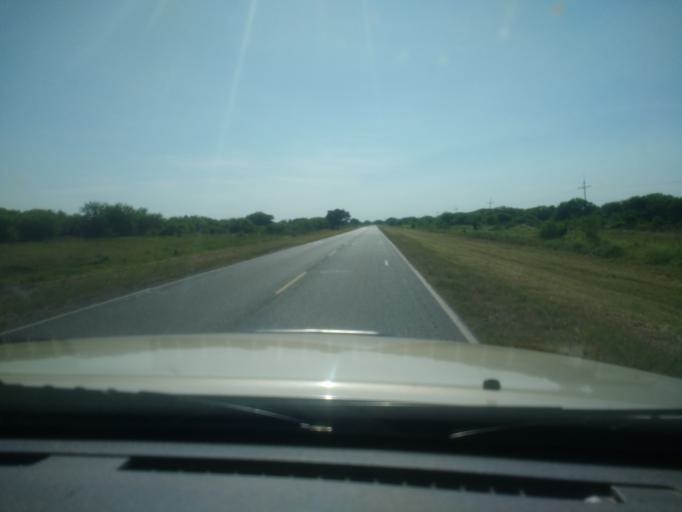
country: PY
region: Presidente Hayes
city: Benjamin Aceval
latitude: -24.9218
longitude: -57.5825
